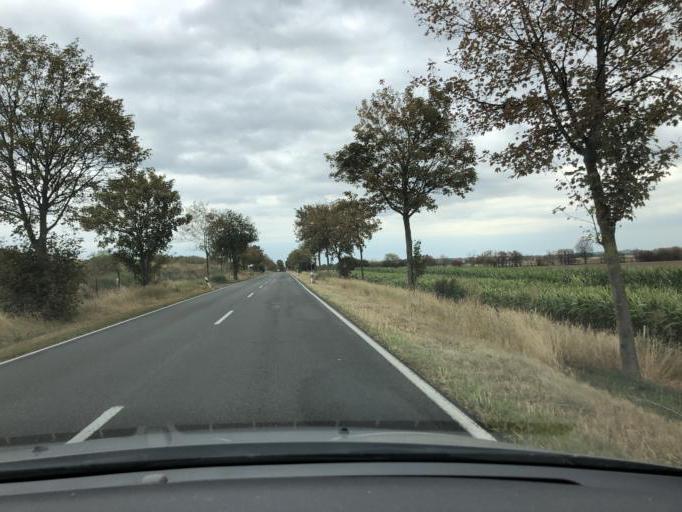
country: DE
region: Saxony-Anhalt
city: Nienburg/Saale
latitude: 51.8442
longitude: 11.7345
